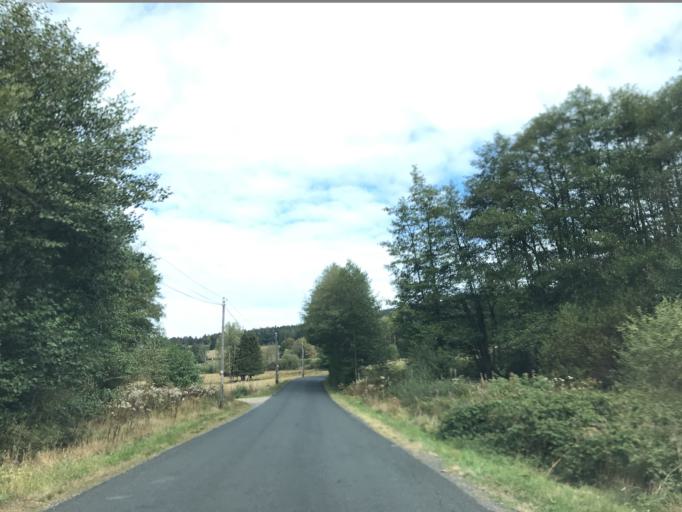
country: FR
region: Auvergne
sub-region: Departement du Puy-de-Dome
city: Celles-sur-Durolle
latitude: 45.7890
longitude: 3.6729
